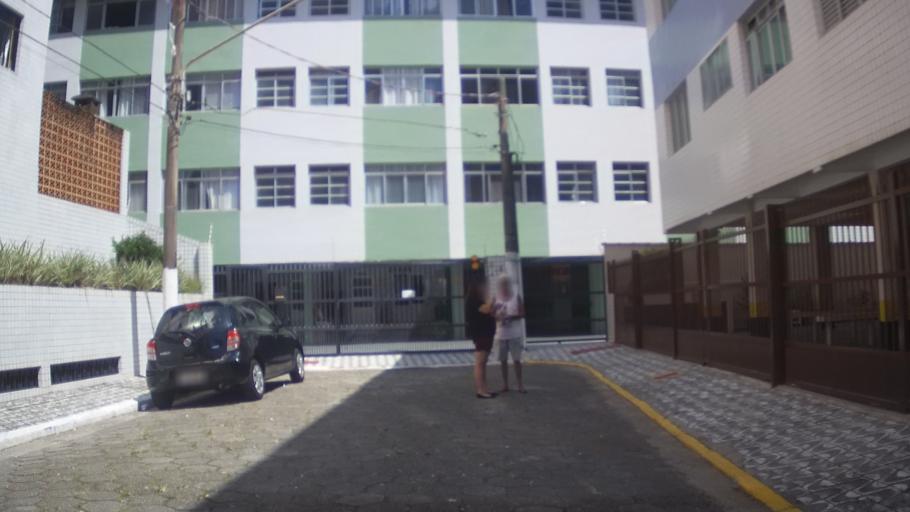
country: BR
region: Sao Paulo
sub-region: Praia Grande
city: Praia Grande
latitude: -24.0168
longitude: -46.4398
